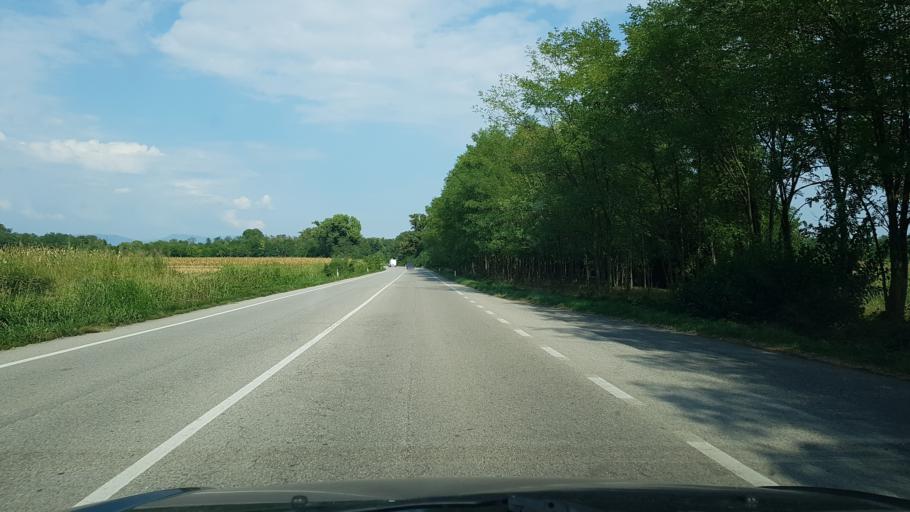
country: IT
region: Friuli Venezia Giulia
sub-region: Provincia di Udine
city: Colloredo di Prato
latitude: 46.0572
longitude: 13.1576
